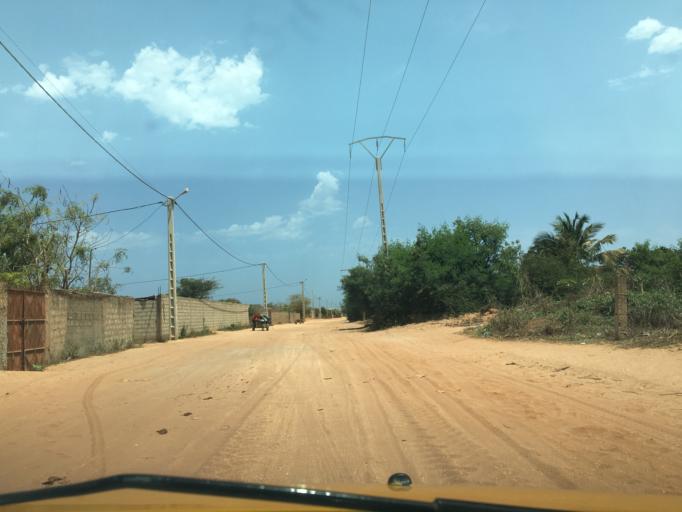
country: SN
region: Thies
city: Thies
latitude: 14.8096
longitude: -17.1900
